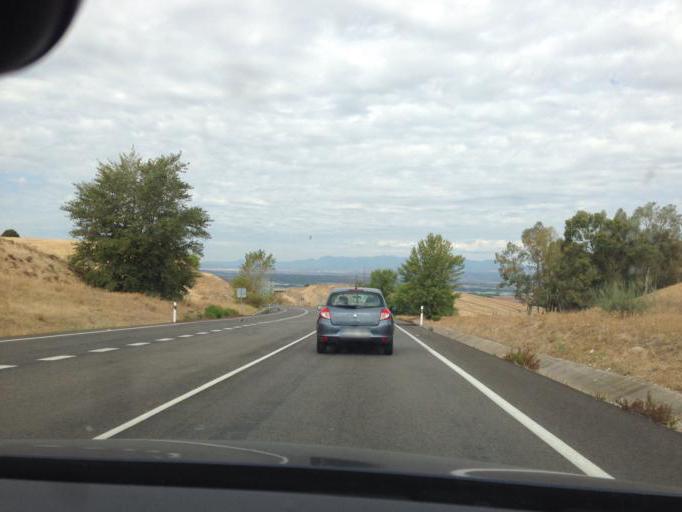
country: ES
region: Madrid
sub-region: Provincia de Madrid
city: Cobena
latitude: 40.5553
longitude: -3.5019
